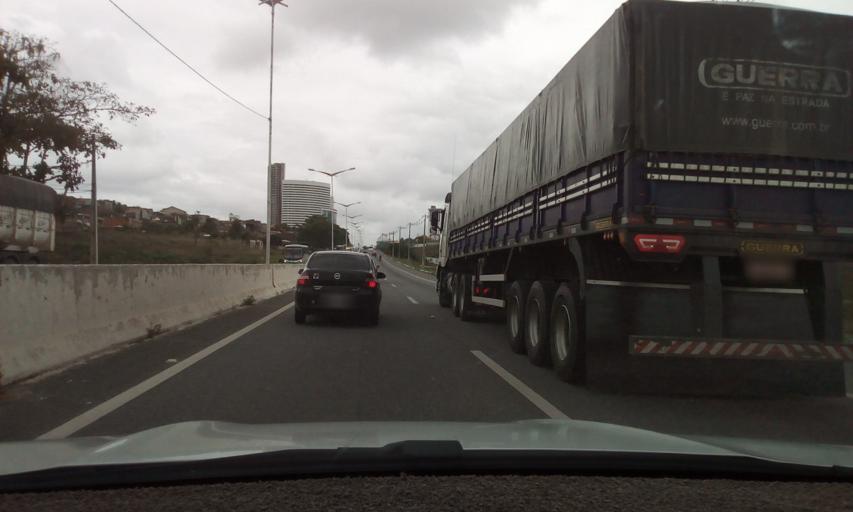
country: BR
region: Paraiba
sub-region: Campina Grande
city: Campina Grande
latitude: -7.2413
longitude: -35.8592
